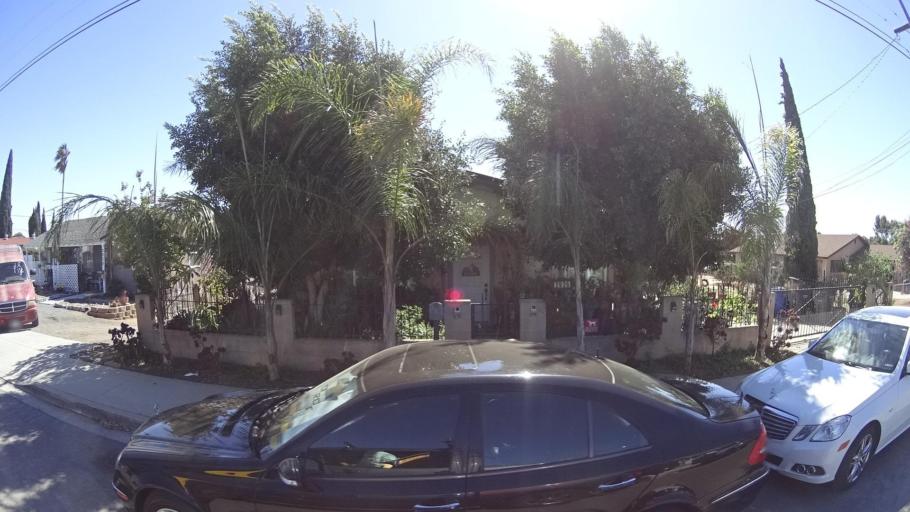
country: US
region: California
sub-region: San Diego County
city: Chula Vista
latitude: 32.6648
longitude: -117.0687
